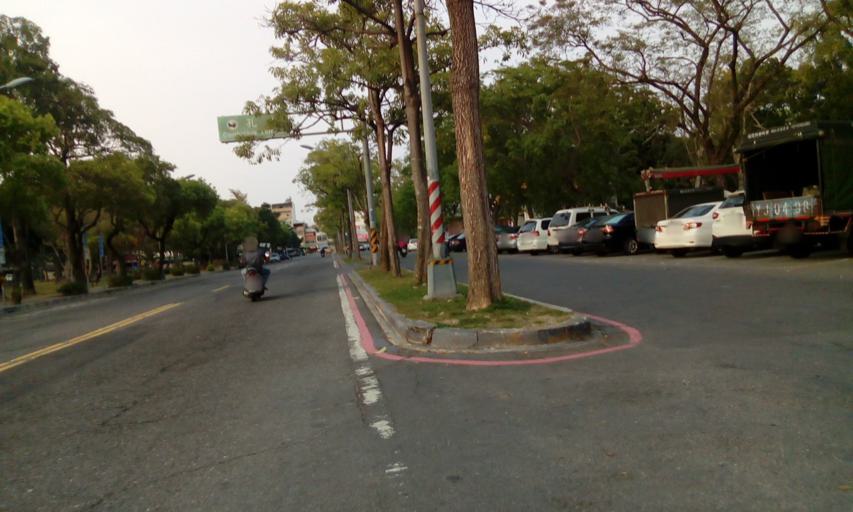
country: TW
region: Kaohsiung
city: Kaohsiung
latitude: 22.6880
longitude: 120.2977
